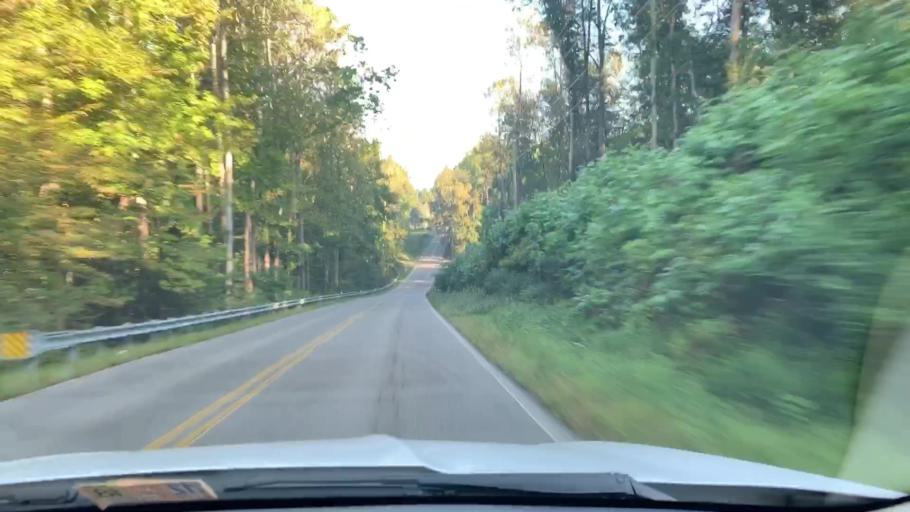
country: US
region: Virginia
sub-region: Middlesex County
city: Deltaville
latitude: 37.5643
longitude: -76.4519
